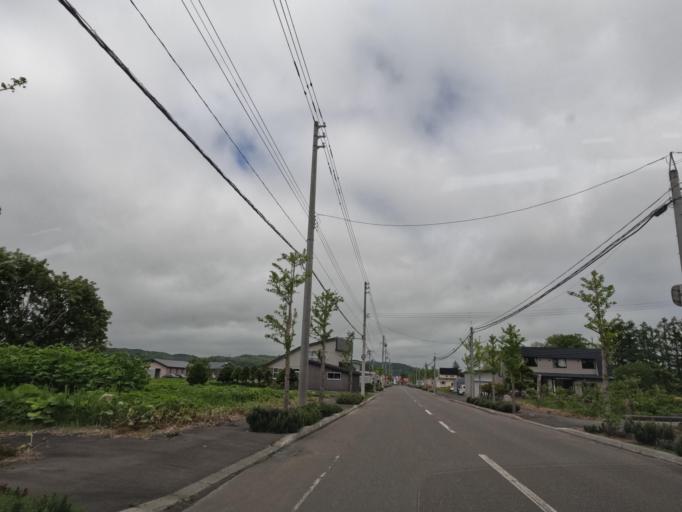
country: JP
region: Hokkaido
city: Tobetsu
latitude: 43.2348
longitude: 141.5146
